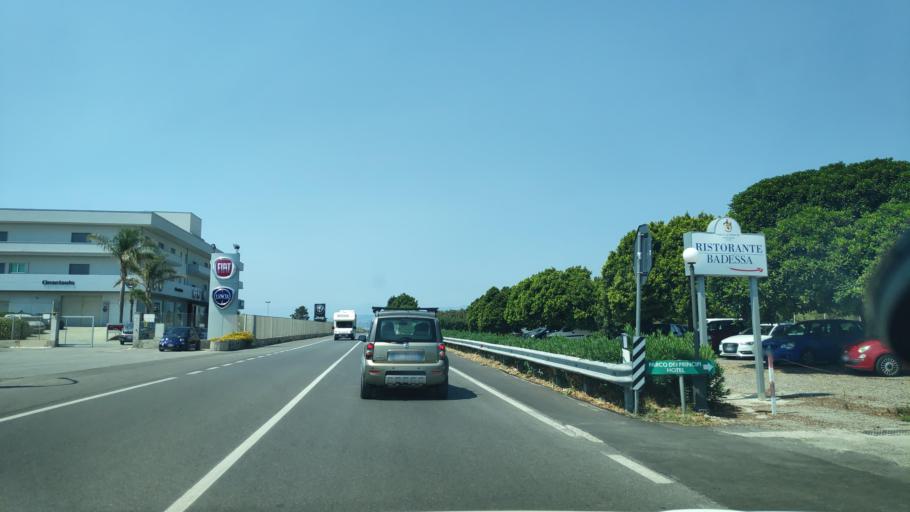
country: IT
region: Calabria
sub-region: Provincia di Reggio Calabria
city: Roccella Ionica
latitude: 38.3077
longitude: 16.3623
